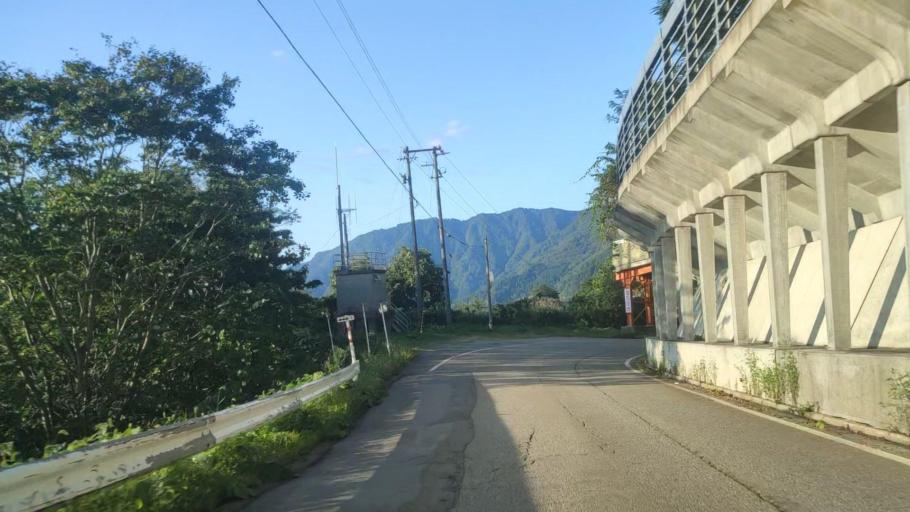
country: JP
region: Toyama
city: Yatsuomachi-higashikumisaka
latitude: 36.5070
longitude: 137.0219
